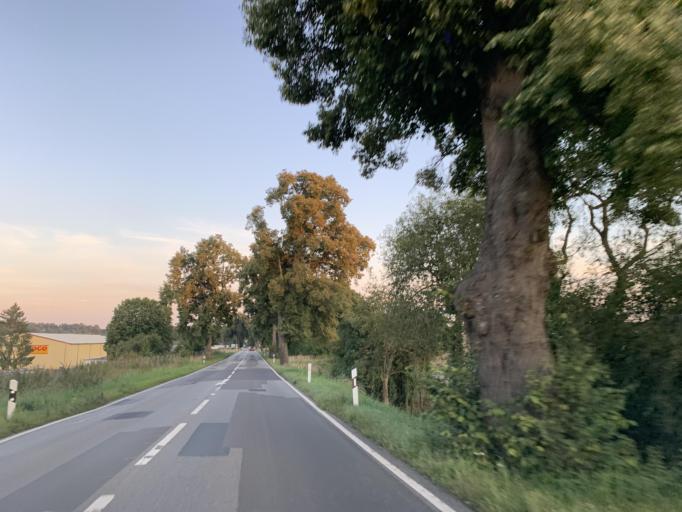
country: DE
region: Mecklenburg-Vorpommern
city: Burg Stargard
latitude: 53.5060
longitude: 13.2937
